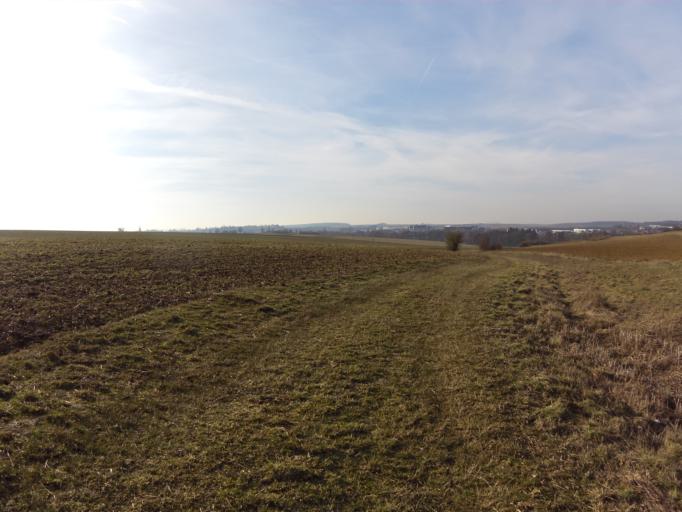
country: DE
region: Bavaria
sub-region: Regierungsbezirk Unterfranken
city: Kurnach
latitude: 49.8345
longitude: 10.0293
